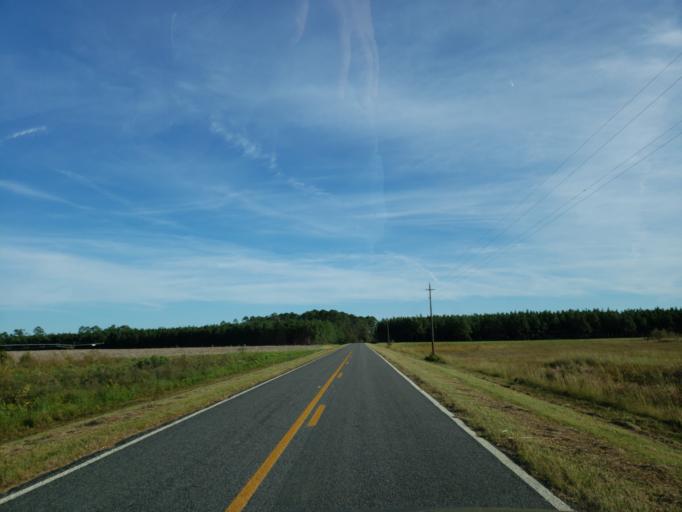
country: US
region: Georgia
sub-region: Dooly County
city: Vienna
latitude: 32.0489
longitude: -83.7589
